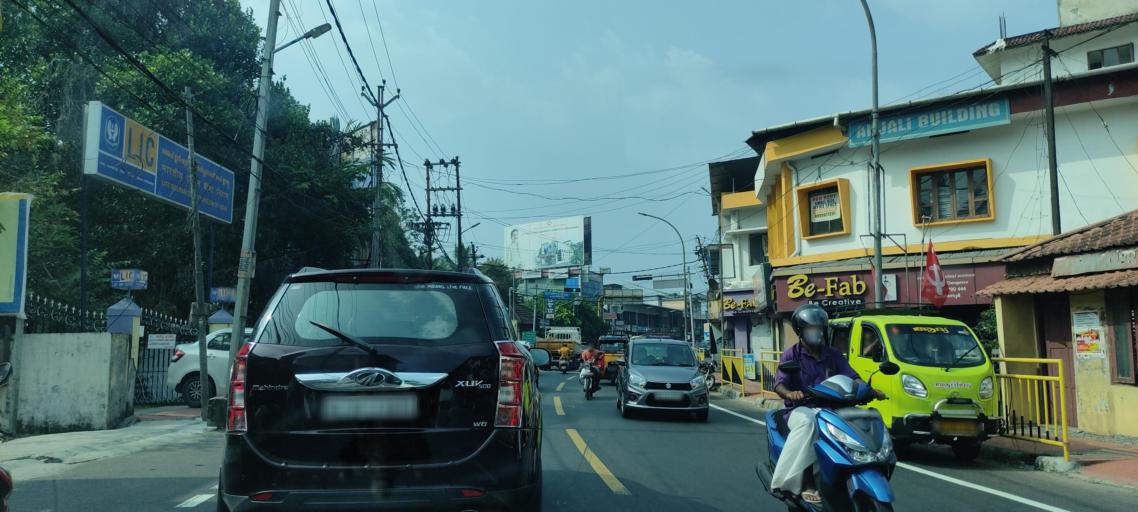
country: IN
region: Kerala
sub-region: Alappuzha
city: Chengannur
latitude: 9.3203
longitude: 76.6106
